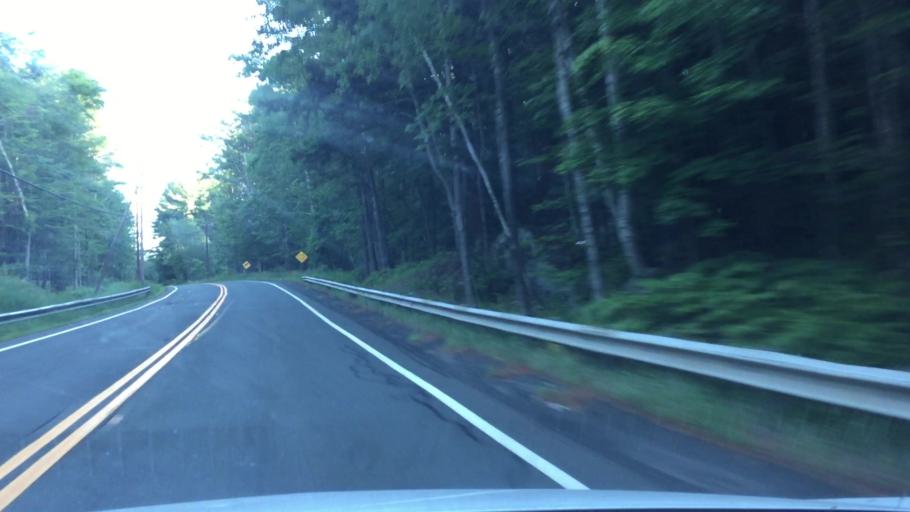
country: US
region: Massachusetts
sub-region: Berkshire County
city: Otis
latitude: 42.2231
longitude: -73.1050
